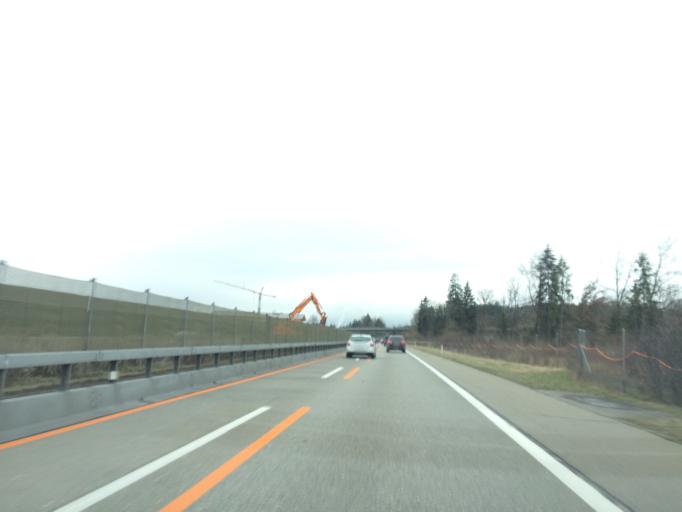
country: CH
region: Bern
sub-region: Bern-Mittelland District
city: Niederwichtrach
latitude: 46.8387
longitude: 7.5602
